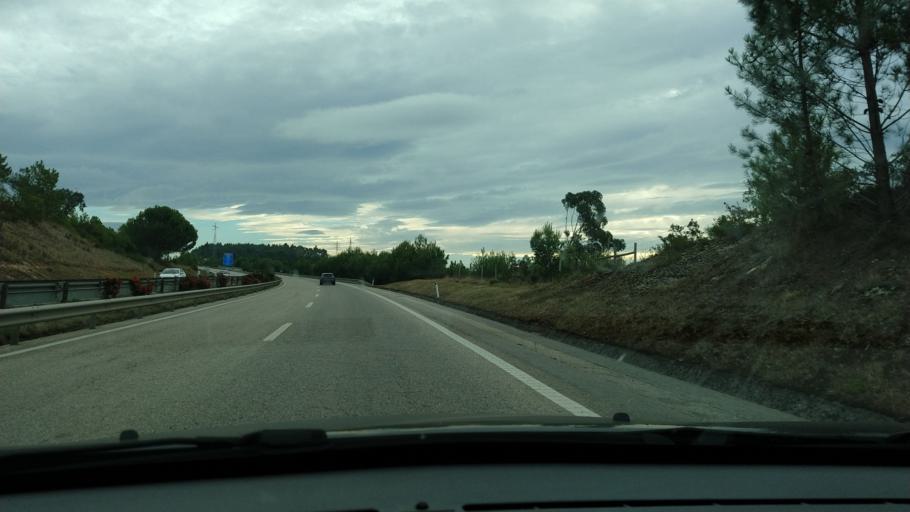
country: PT
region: Coimbra
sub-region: Figueira da Foz
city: Tavarede
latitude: 40.1498
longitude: -8.8216
